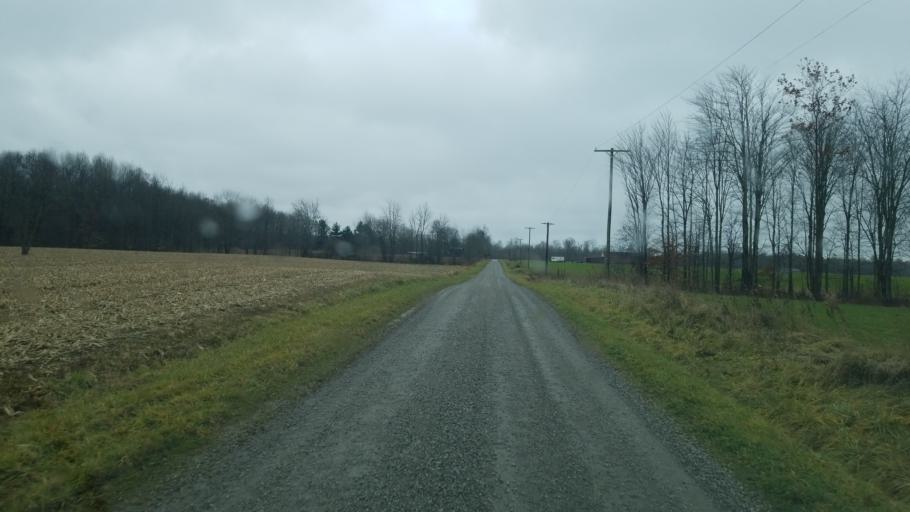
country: US
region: Ohio
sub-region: Ashtabula County
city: Roaming Shores
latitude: 41.5618
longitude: -80.7194
